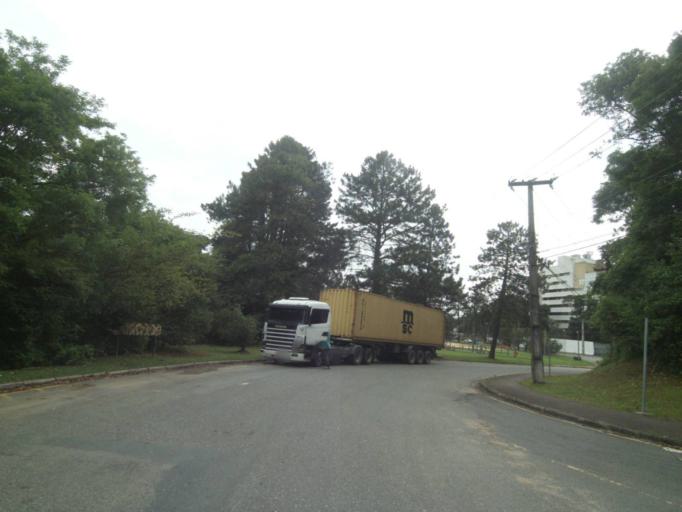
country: BR
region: Parana
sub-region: Curitiba
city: Curitiba
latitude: -25.4092
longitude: -49.3063
